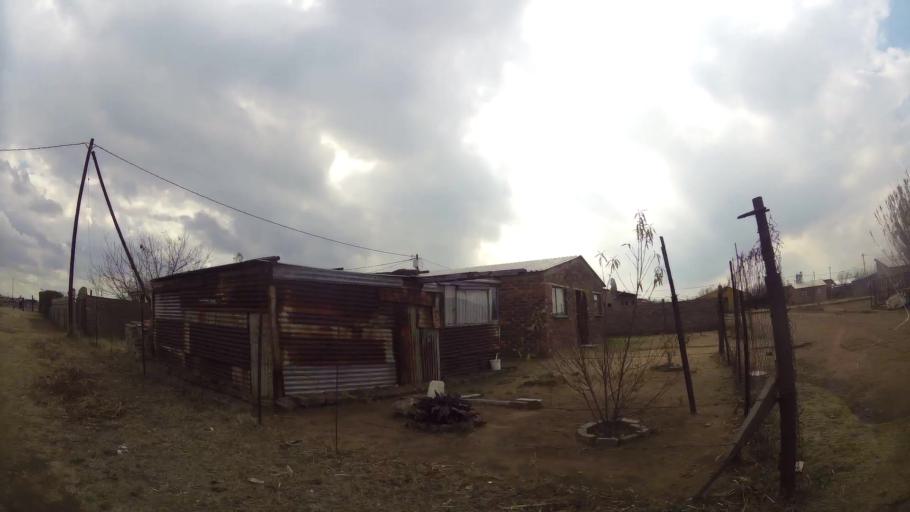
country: ZA
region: Orange Free State
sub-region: Fezile Dabi District Municipality
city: Sasolburg
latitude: -26.8631
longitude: 27.8995
